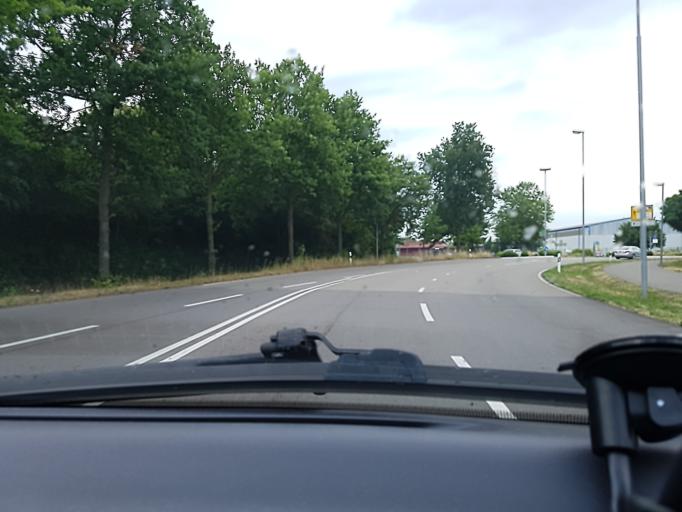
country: DE
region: Baden-Wuerttemberg
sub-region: Freiburg Region
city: Kehl
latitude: 48.5510
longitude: 7.8360
